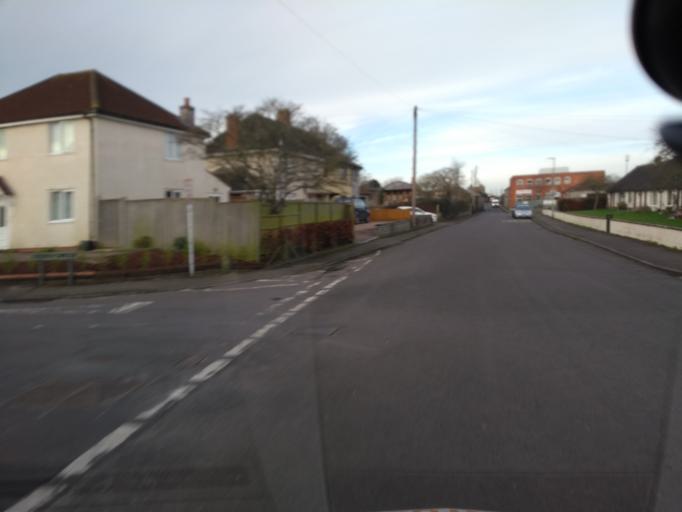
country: GB
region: England
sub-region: Somerset
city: Street
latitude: 51.1207
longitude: -2.7374
